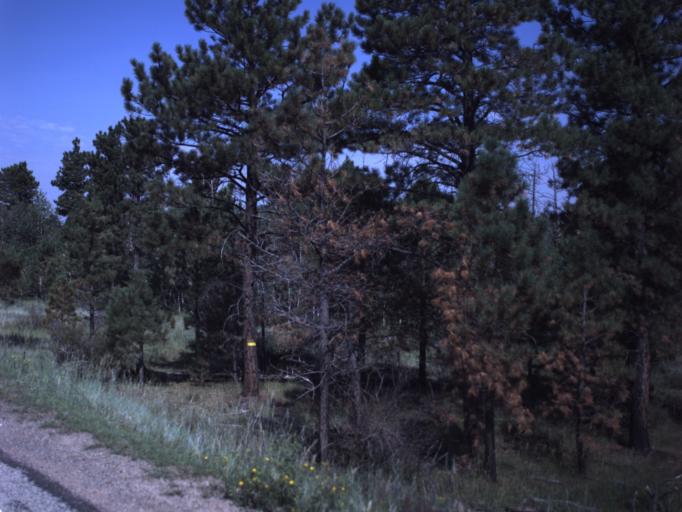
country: US
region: Utah
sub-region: Daggett County
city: Manila
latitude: 40.8600
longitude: -109.5499
